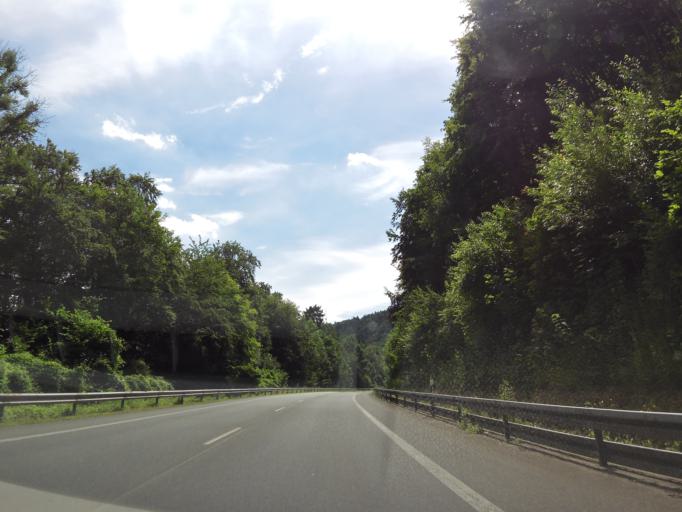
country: DE
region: North Rhine-Westphalia
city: Beverungen
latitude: 51.6385
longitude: 9.3787
